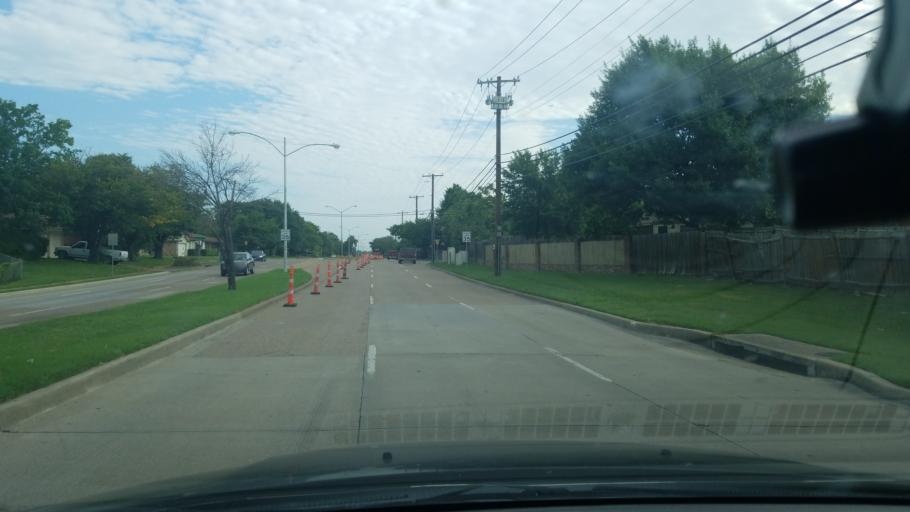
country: US
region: Texas
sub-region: Dallas County
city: Balch Springs
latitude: 32.7387
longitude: -96.6656
